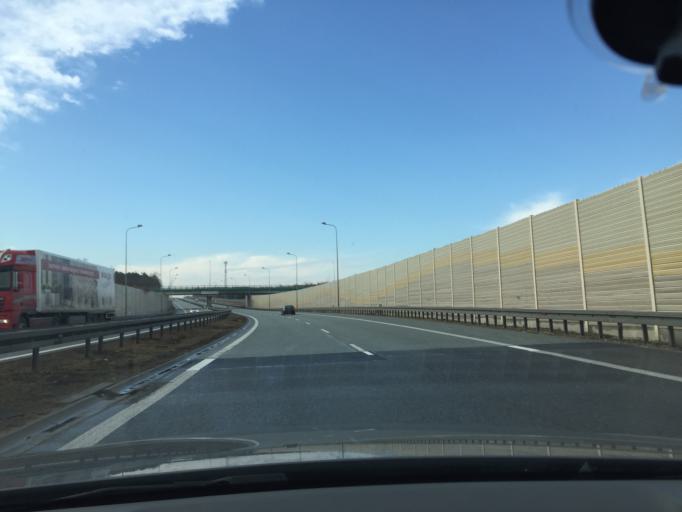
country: PL
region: Lodz Voivodeship
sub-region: Powiat rawski
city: Rawa Mazowiecka
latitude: 51.8273
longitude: 20.3259
